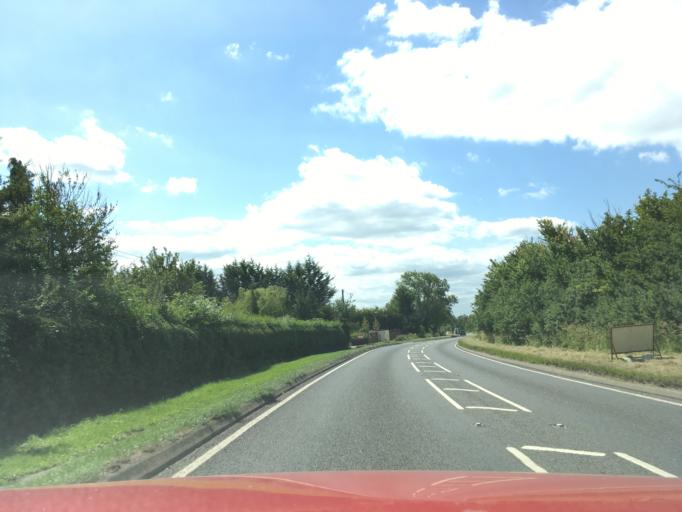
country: GB
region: England
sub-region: Buckinghamshire
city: Aylesbury
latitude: 51.8714
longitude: -0.8321
